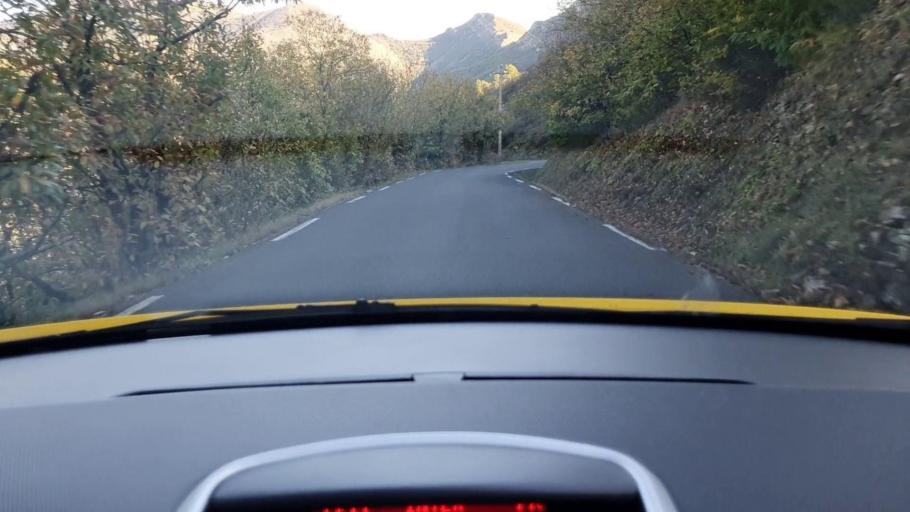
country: FR
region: Languedoc-Roussillon
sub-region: Departement du Gard
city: Sumene
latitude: 43.9859
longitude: 3.7044
